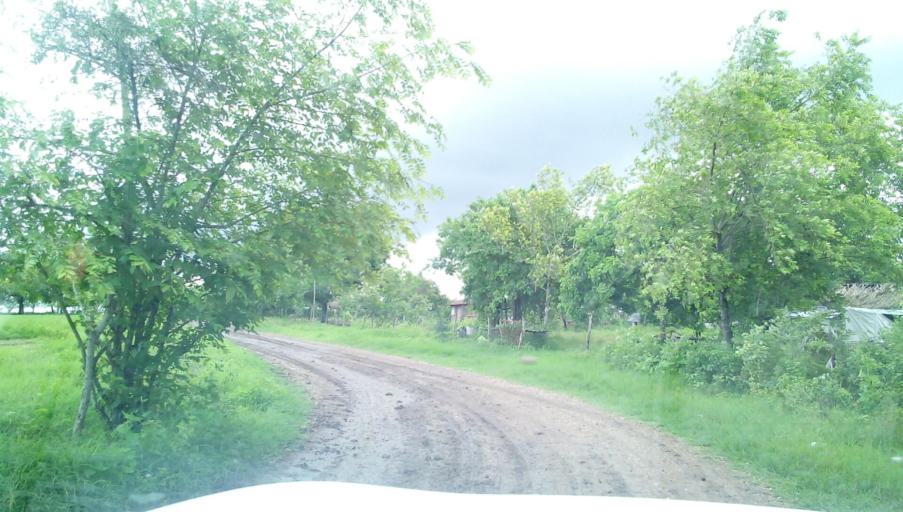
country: MX
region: Veracruz
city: Panuco
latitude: 21.7991
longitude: -98.0988
